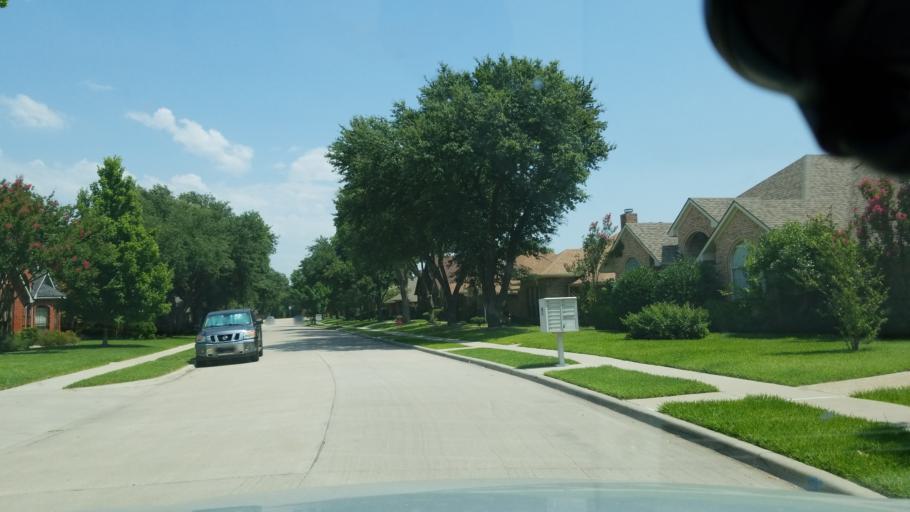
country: US
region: Texas
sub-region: Dallas County
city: Coppell
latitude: 32.9676
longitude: -96.9815
